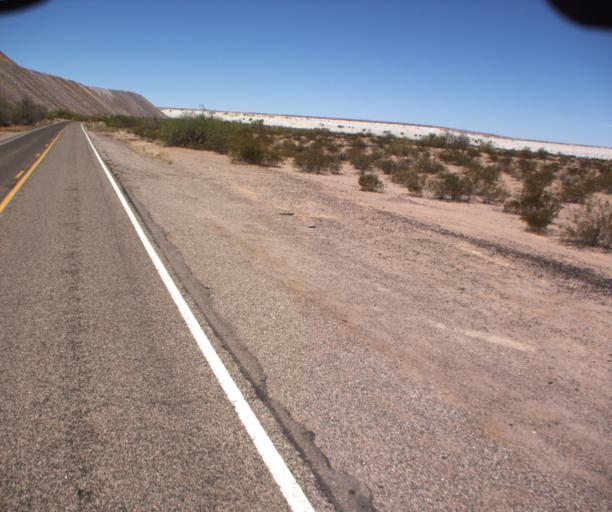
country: US
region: Arizona
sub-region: Pima County
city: Ajo
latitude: 32.3565
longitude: -112.8278
